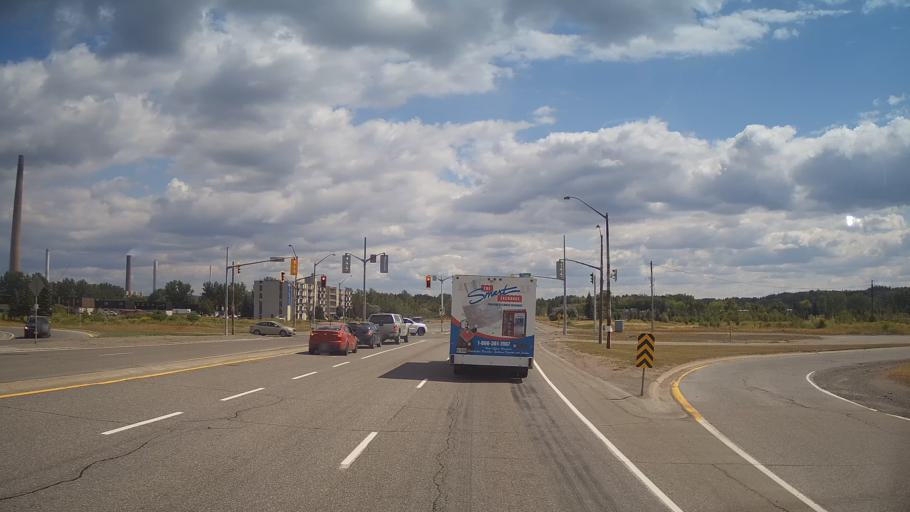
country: CA
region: Ontario
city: Greater Sudbury
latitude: 46.4652
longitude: -81.0750
